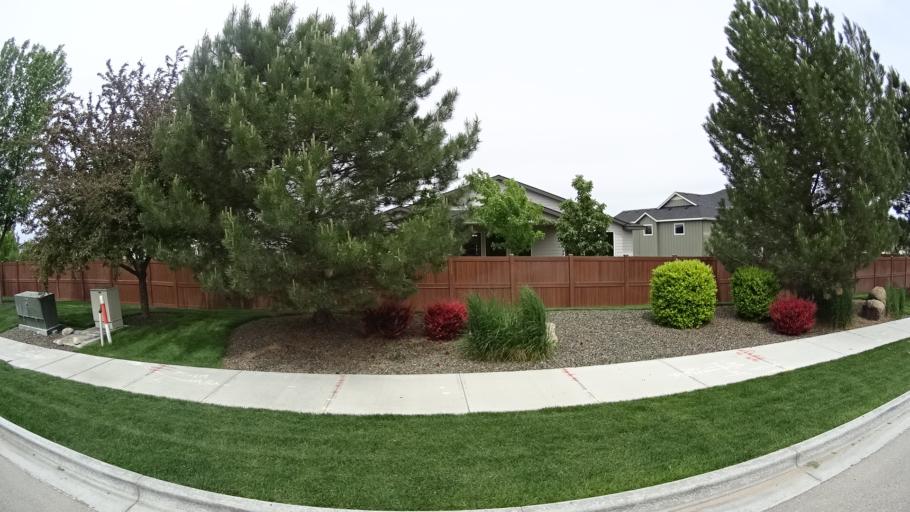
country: US
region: Idaho
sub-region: Ada County
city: Meridian
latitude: 43.5538
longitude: -116.3616
